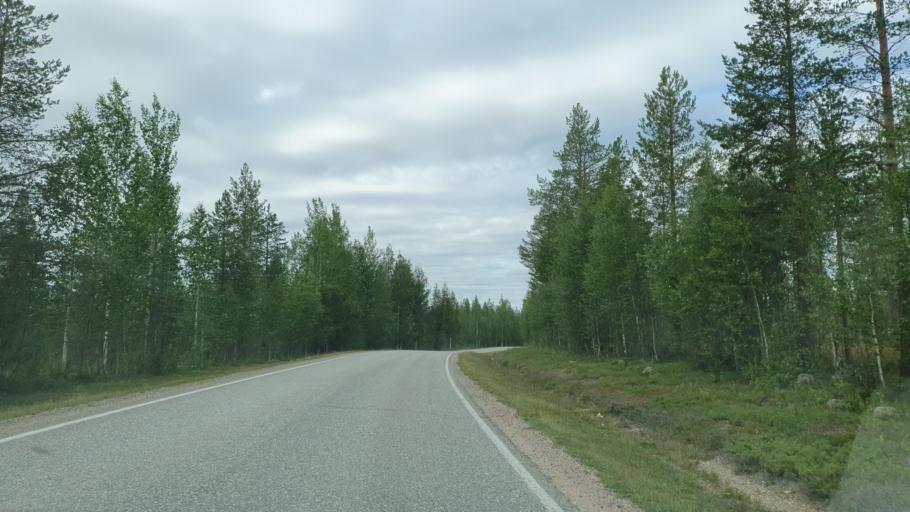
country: FI
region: Lapland
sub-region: Tunturi-Lappi
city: Kittilae
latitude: 67.6080
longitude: 25.2730
